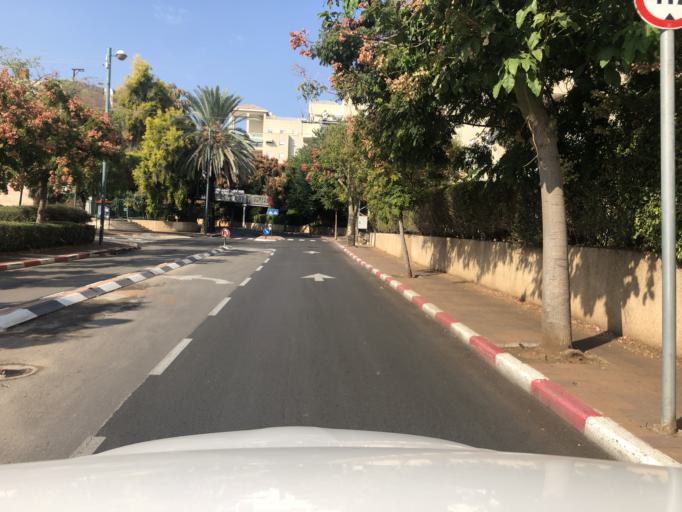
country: IL
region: Central District
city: Kfar Saba
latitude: 32.1789
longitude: 34.9058
